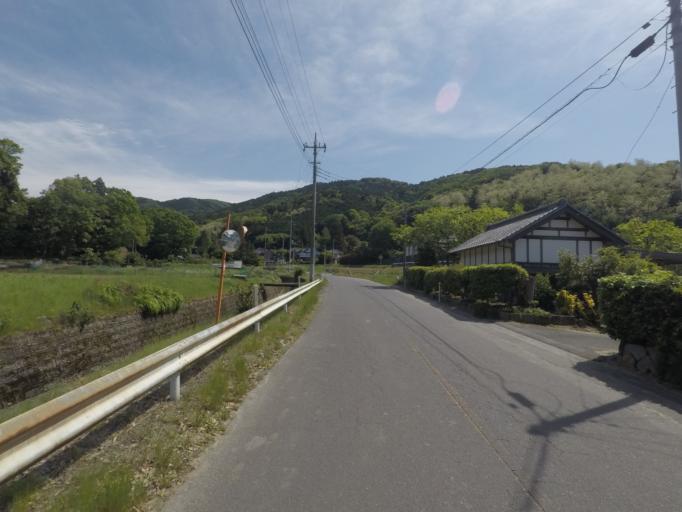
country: JP
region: Ibaraki
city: Makabe
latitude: 36.2604
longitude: 140.1054
